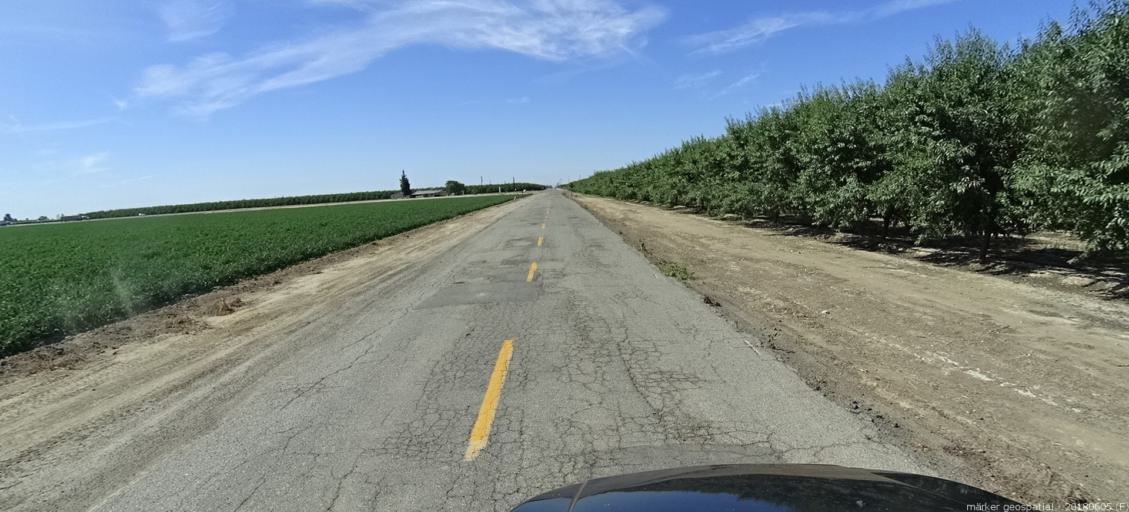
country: US
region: California
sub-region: Madera County
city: Chowchilla
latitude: 37.0868
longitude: -120.4008
